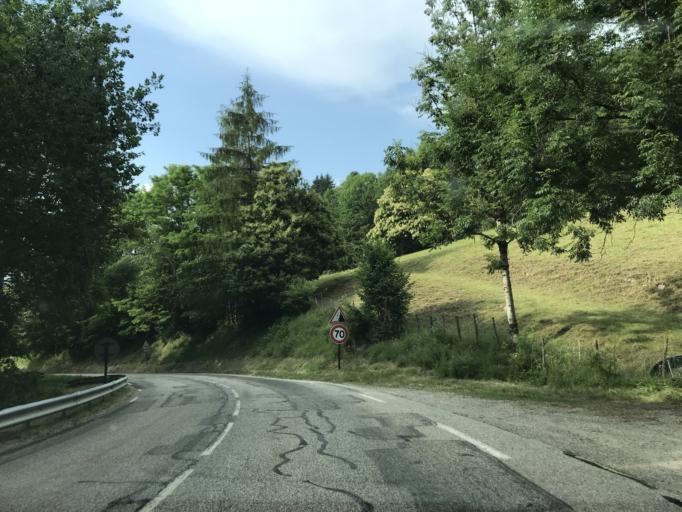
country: FR
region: Rhone-Alpes
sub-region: Departement de l'Isere
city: Allevard
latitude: 45.3820
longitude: 6.0868
